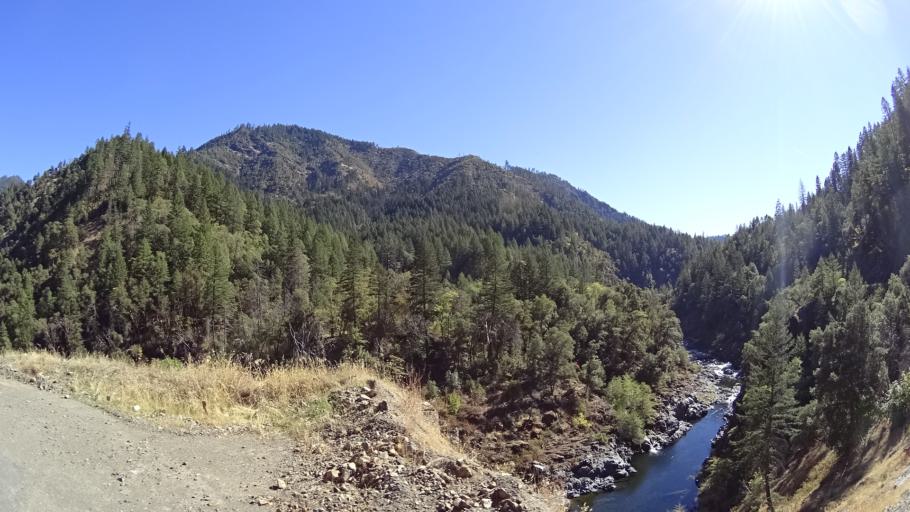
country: US
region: California
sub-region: Humboldt County
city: Willow Creek
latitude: 41.3194
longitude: -123.3821
